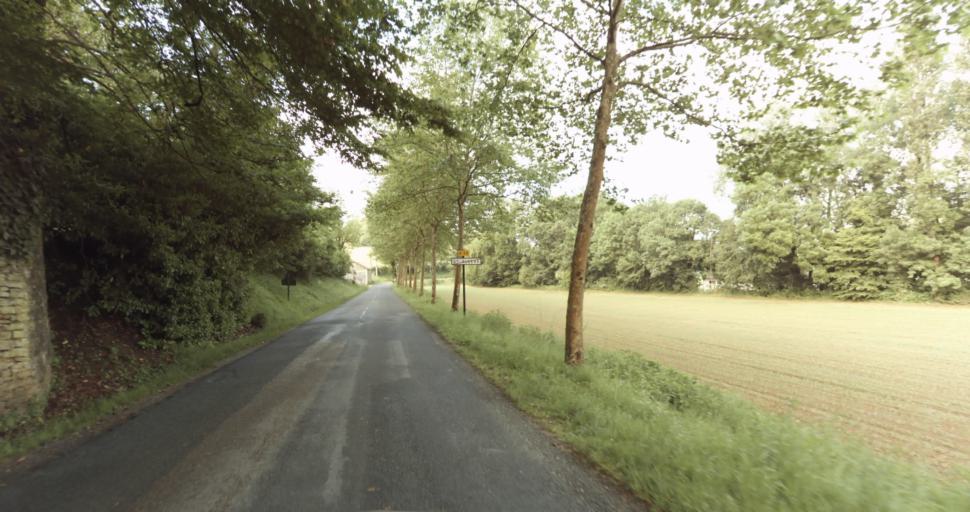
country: FR
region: Aquitaine
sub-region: Departement de la Dordogne
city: Vergt
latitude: 44.9442
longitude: 0.8063
